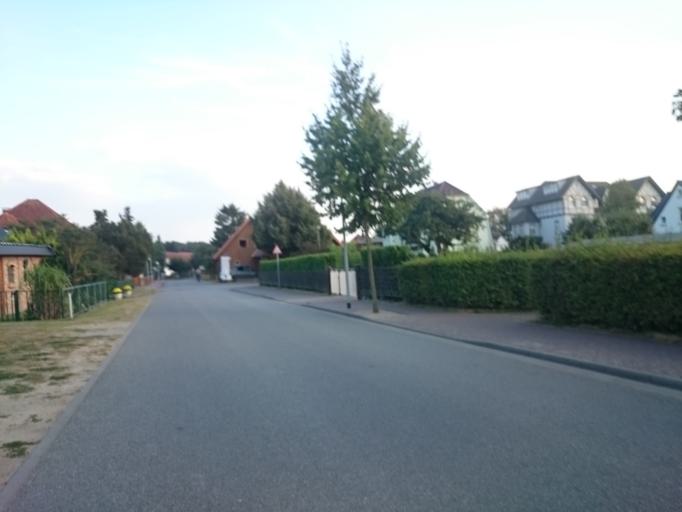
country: DE
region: Mecklenburg-Vorpommern
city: Koserow
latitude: 54.0502
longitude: 14.0048
